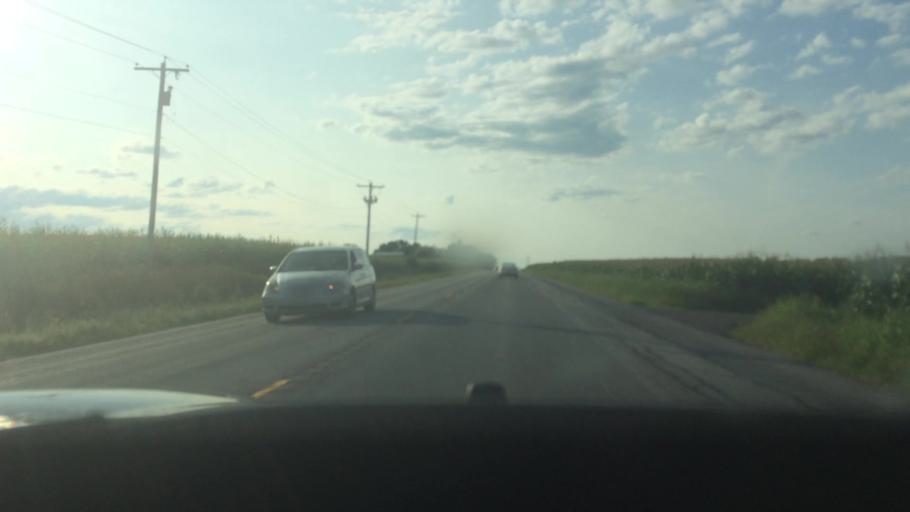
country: US
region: New York
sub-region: St. Lawrence County
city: Canton
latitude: 44.5995
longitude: -75.1948
